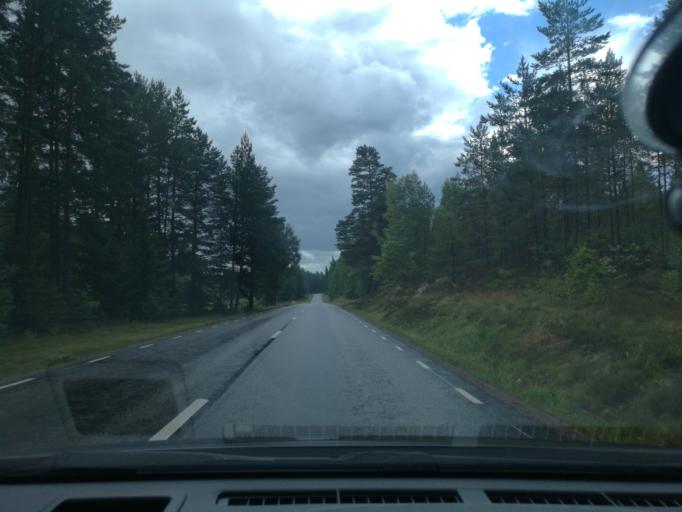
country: SE
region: OEstergoetland
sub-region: Motala Kommun
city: Borensberg
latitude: 58.7501
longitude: 15.3788
